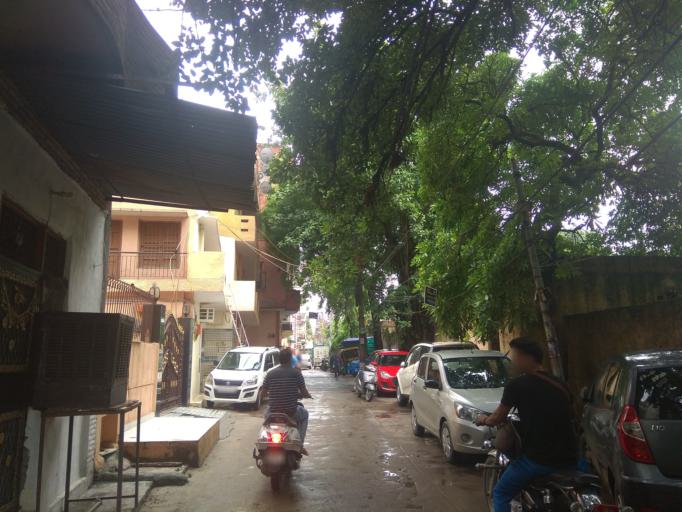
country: IN
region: NCT
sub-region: New Delhi
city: New Delhi
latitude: 28.5728
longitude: 77.2555
